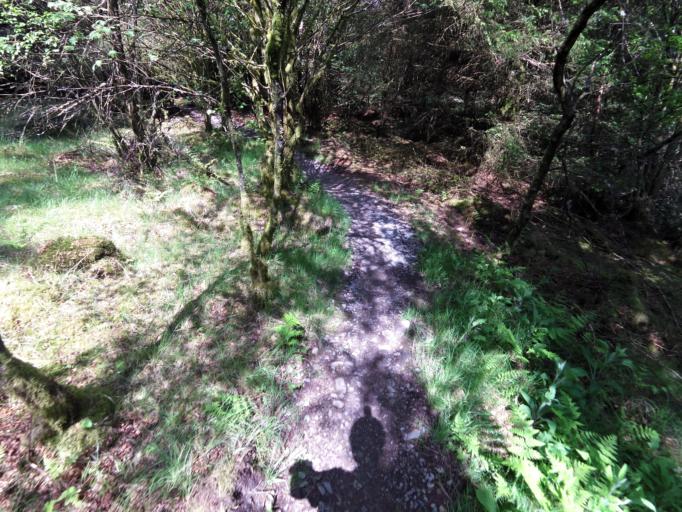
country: GB
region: England
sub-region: Lancashire
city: Clitheroe
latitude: 54.0052
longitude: -2.4013
